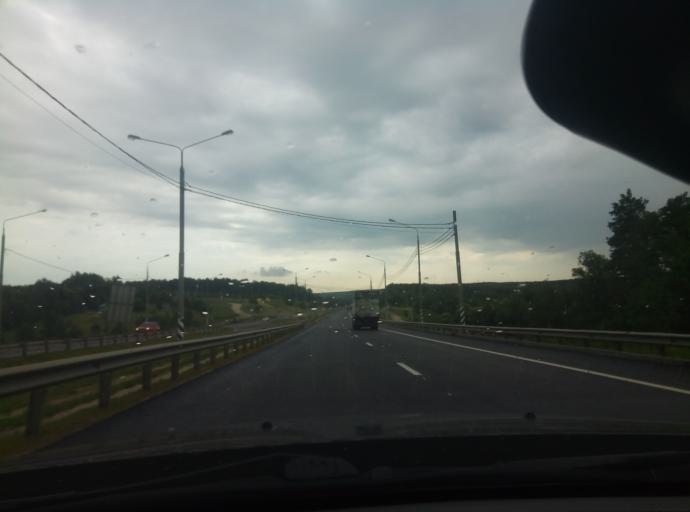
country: RU
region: Tula
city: Zaokskiy
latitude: 54.7766
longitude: 37.4886
